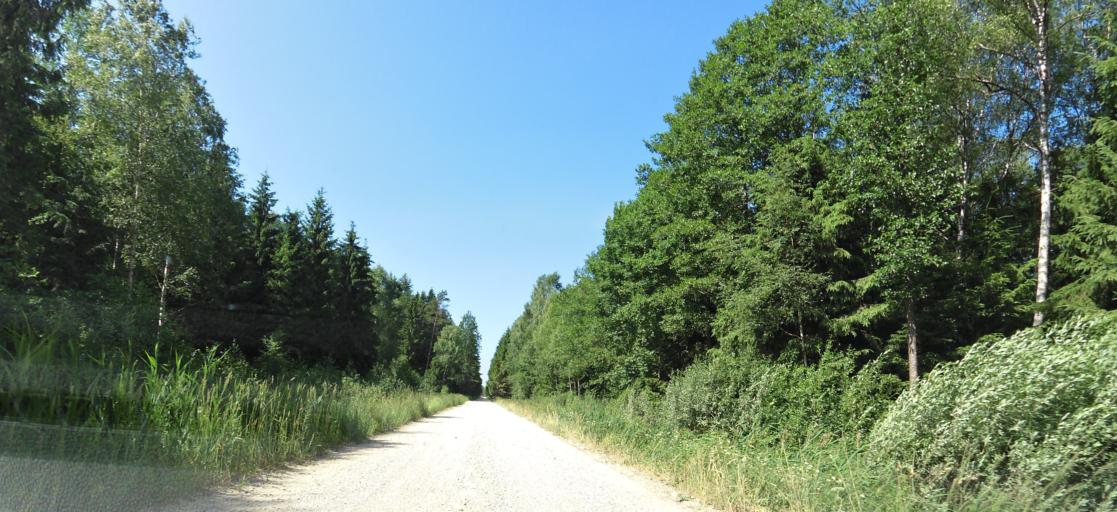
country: LT
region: Panevezys
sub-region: Birzai
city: Birzai
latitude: 56.2153
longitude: 24.9244
